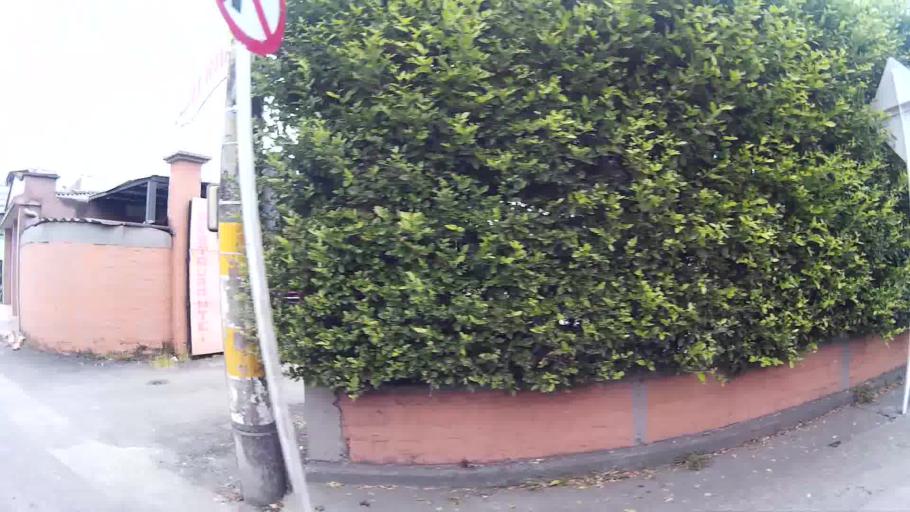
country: CO
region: Risaralda
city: Pereira
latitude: 4.8125
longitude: -75.7342
